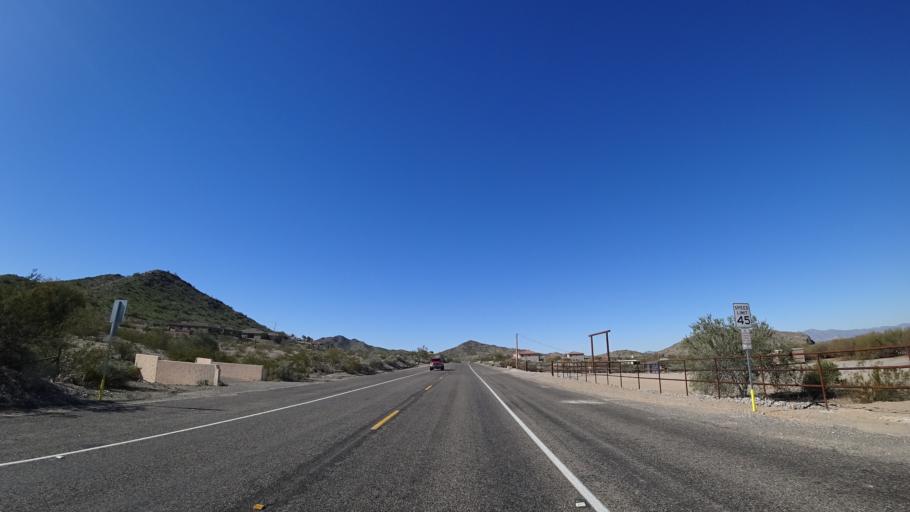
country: US
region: Arizona
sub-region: Maricopa County
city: Goodyear
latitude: 33.3755
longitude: -112.3546
